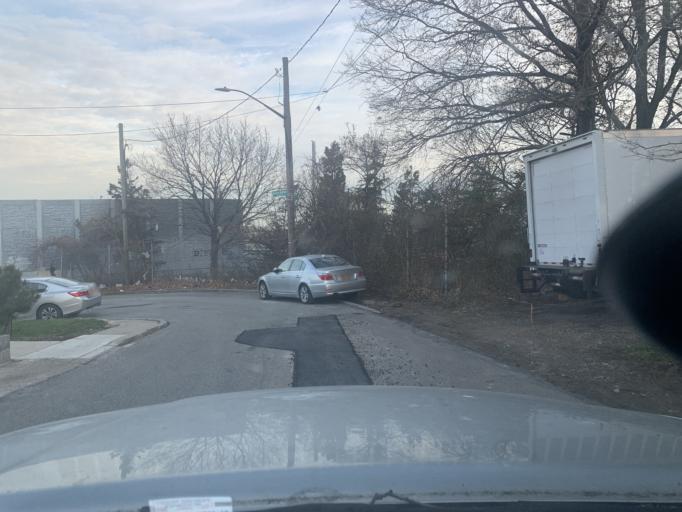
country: US
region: New York
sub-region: Kings County
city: East New York
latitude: 40.7275
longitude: -73.8861
